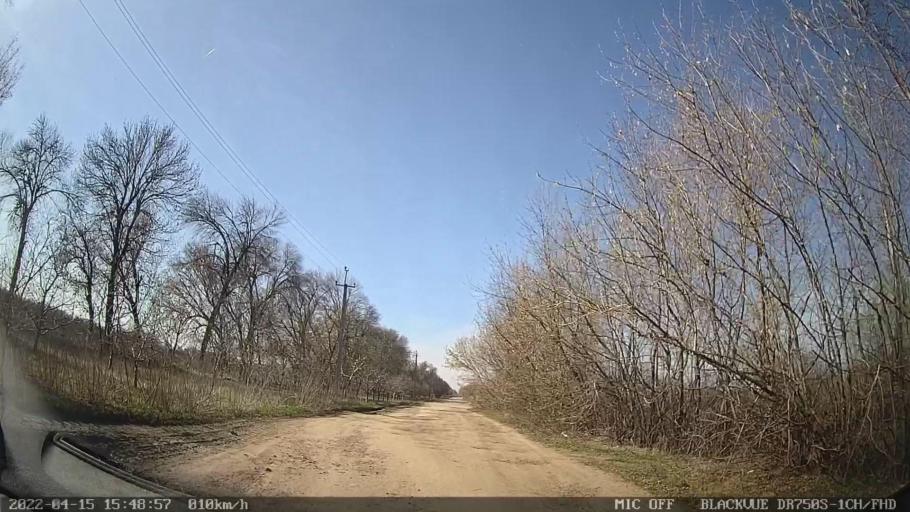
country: MD
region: Raionul Ocnita
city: Otaci
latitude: 48.3881
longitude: 27.9054
